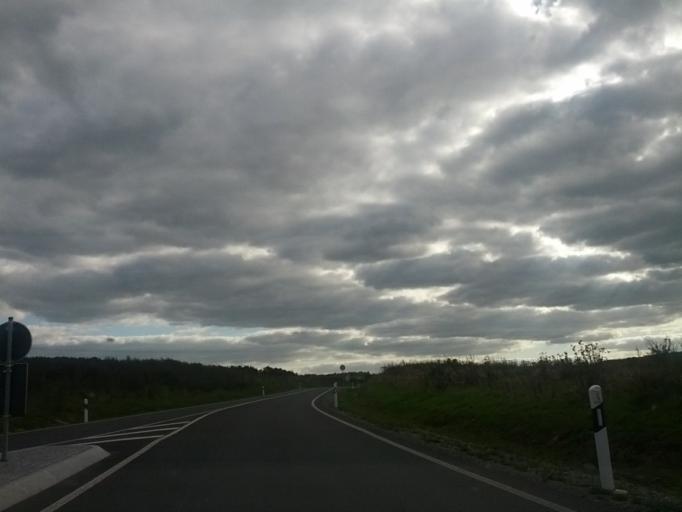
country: DE
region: Thuringia
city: Fambach
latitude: 50.7129
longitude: 10.3681
